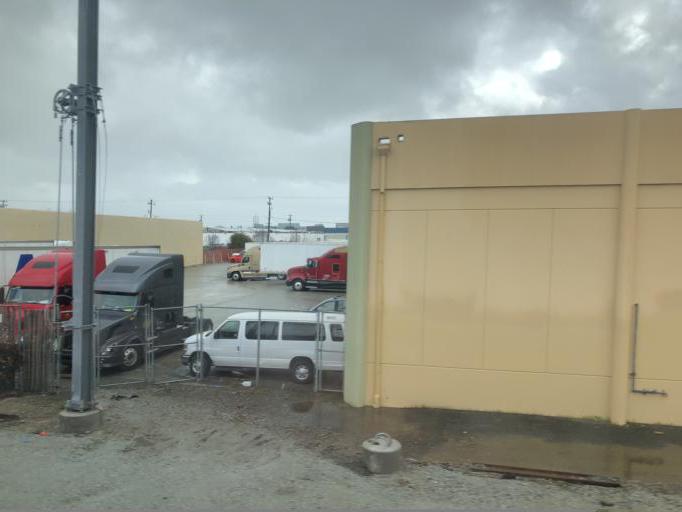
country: US
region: California
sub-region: San Mateo County
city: South San Francisco
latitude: 37.6464
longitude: -122.4122
